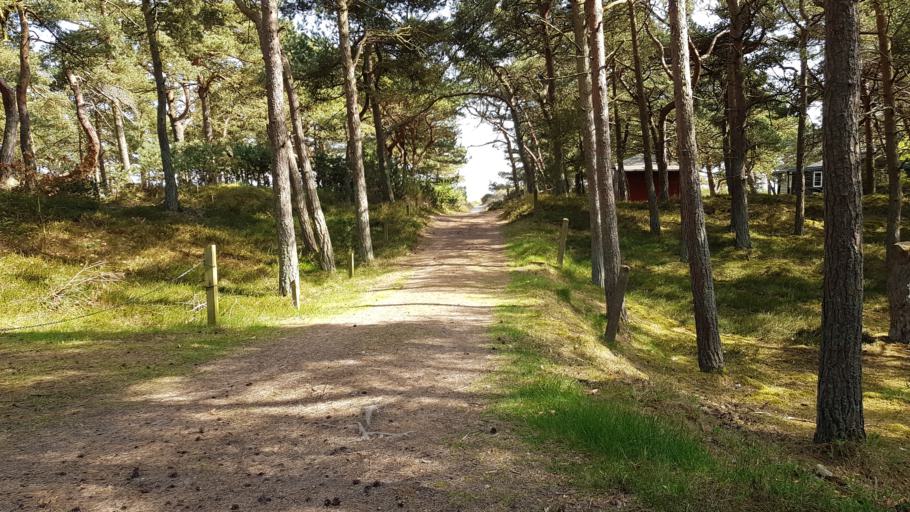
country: DK
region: Capital Region
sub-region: Bornholm Kommune
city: Nexo
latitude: 54.9983
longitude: 15.0900
